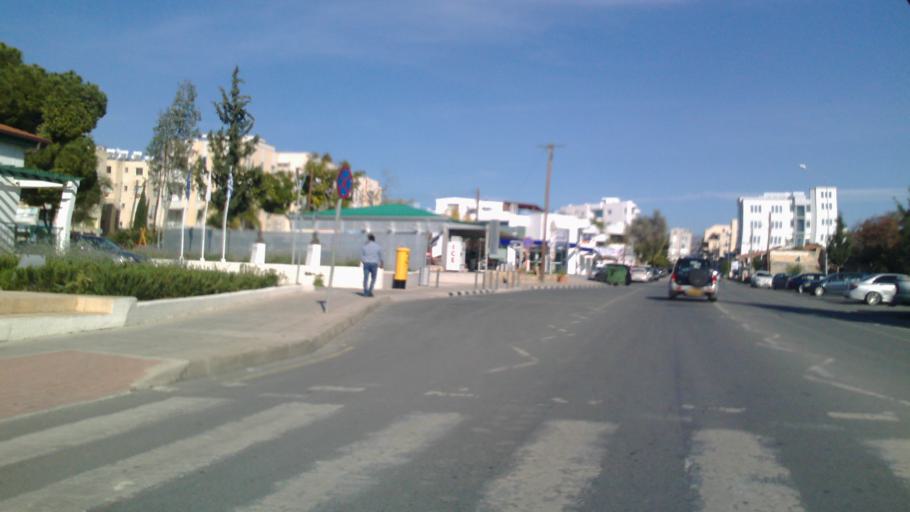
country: CY
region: Pafos
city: Paphos
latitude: 34.7821
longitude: 32.4271
